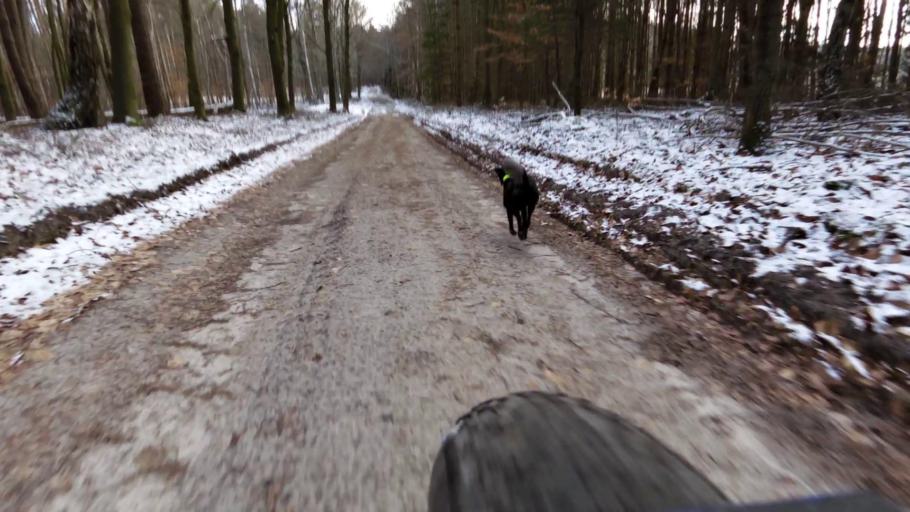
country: PL
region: West Pomeranian Voivodeship
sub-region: Powiat walecki
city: Walcz
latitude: 53.2791
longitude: 16.3063
